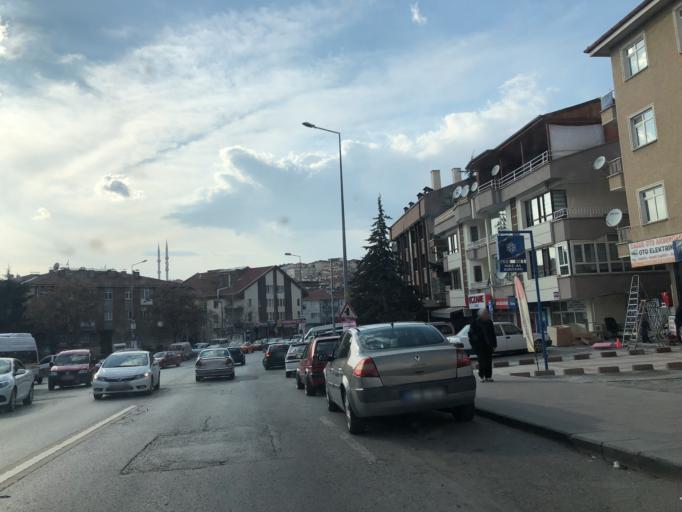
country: TR
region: Ankara
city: Ankara
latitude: 39.9847
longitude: 32.8518
